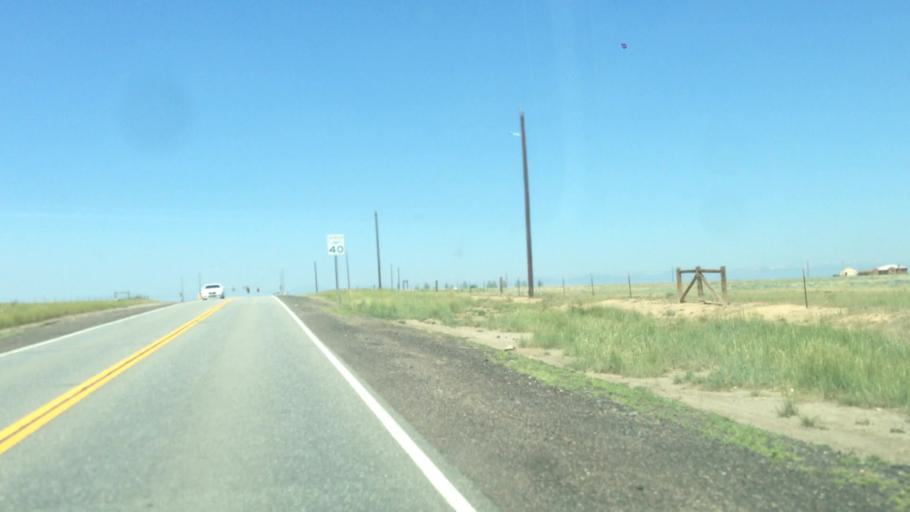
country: US
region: Colorado
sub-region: Arapahoe County
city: Dove Valley
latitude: 39.6530
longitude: -104.7313
